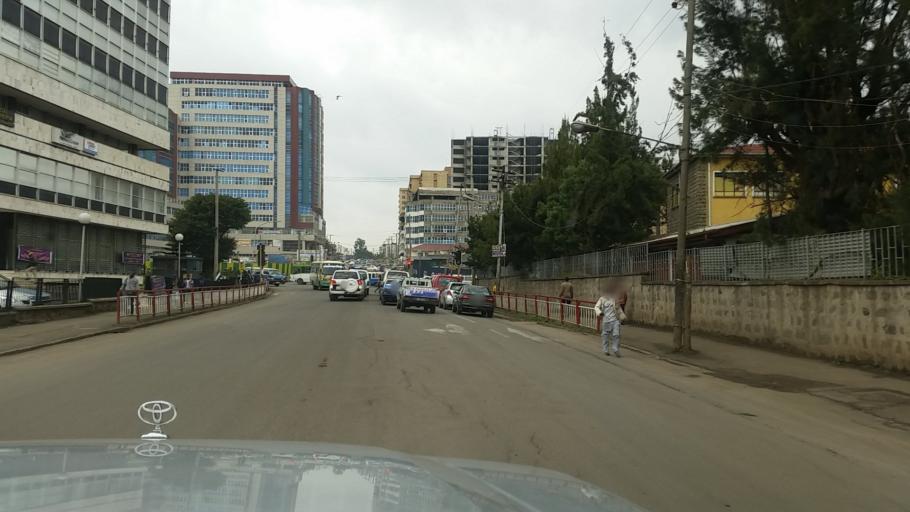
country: ET
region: Adis Abeba
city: Addis Ababa
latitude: 9.0126
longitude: 38.7492
